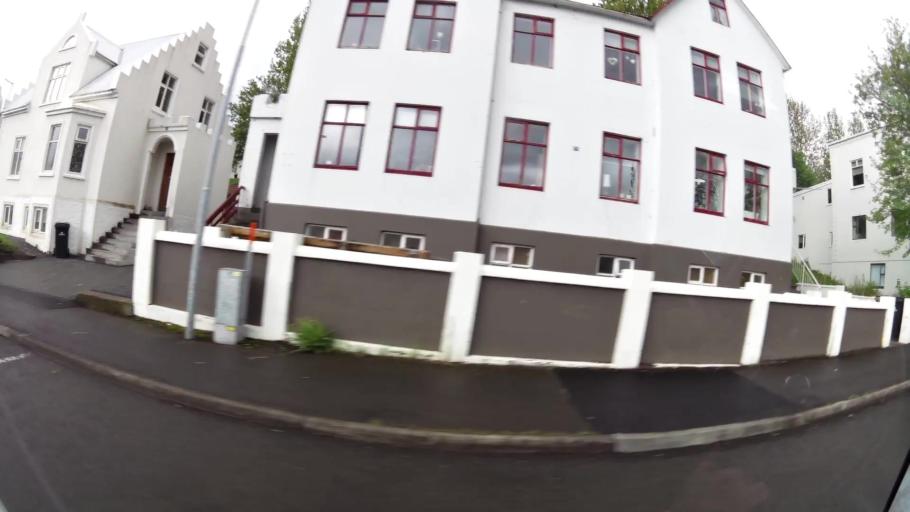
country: IS
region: Northeast
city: Akureyri
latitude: 65.6848
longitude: -18.0962
